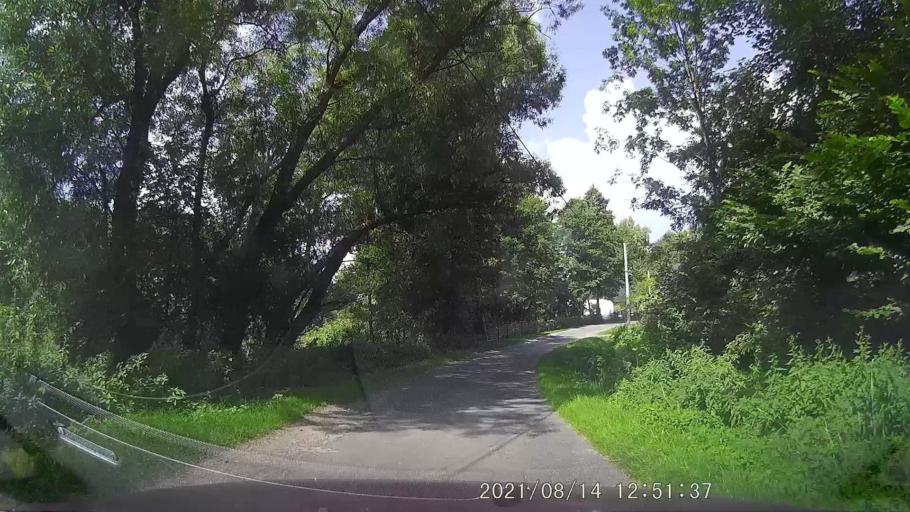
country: PL
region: Lower Silesian Voivodeship
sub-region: Powiat klodzki
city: Stronie Slaskie
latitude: 50.3147
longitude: 16.8315
